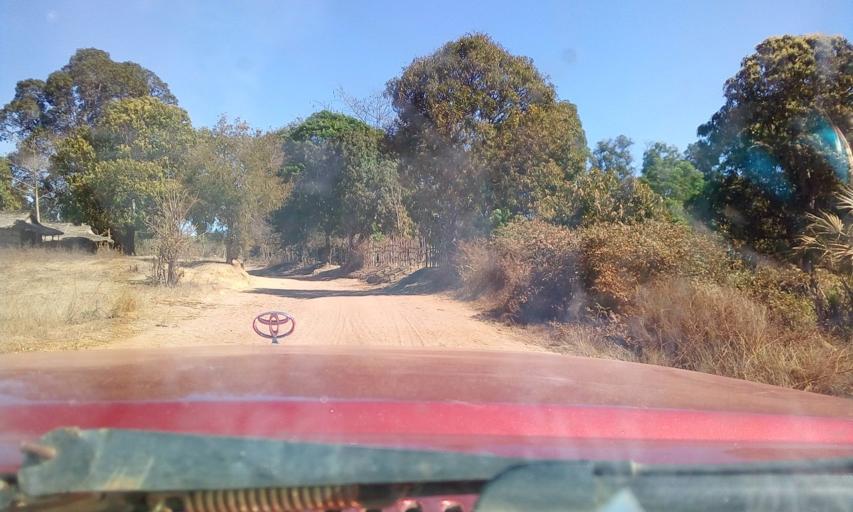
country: MG
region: Boeny
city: Mahajanga
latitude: -15.9609
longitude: 45.9487
